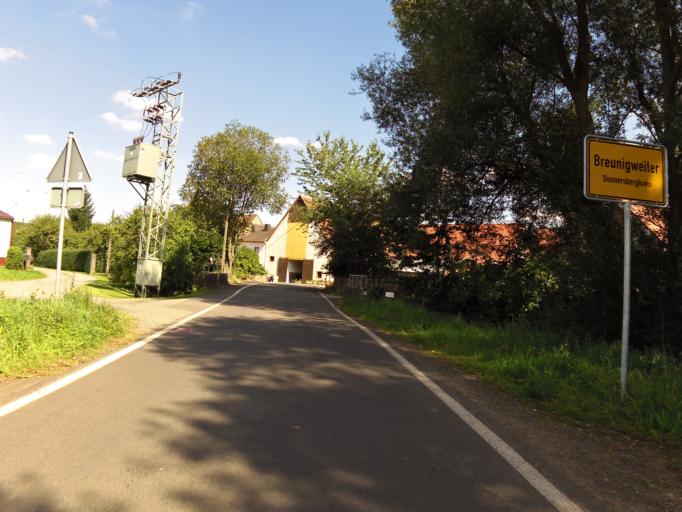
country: DE
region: Rheinland-Pfalz
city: Breunigweiler
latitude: 49.5692
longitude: 7.9618
